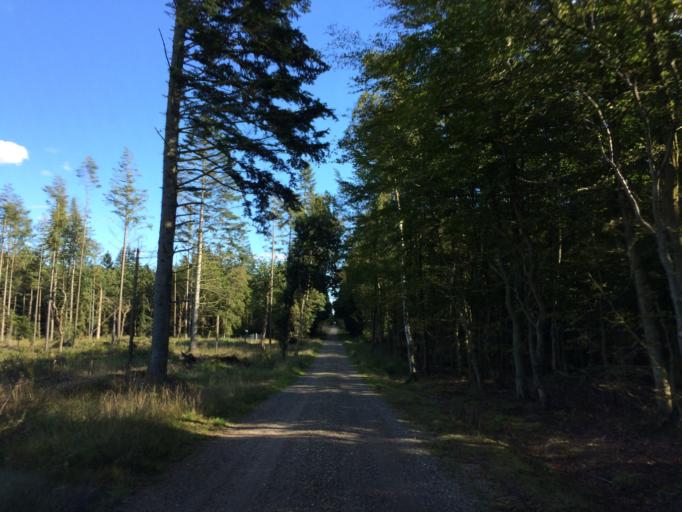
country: DK
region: Central Jutland
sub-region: Holstebro Kommune
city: Ulfborg
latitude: 56.2624
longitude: 8.4388
